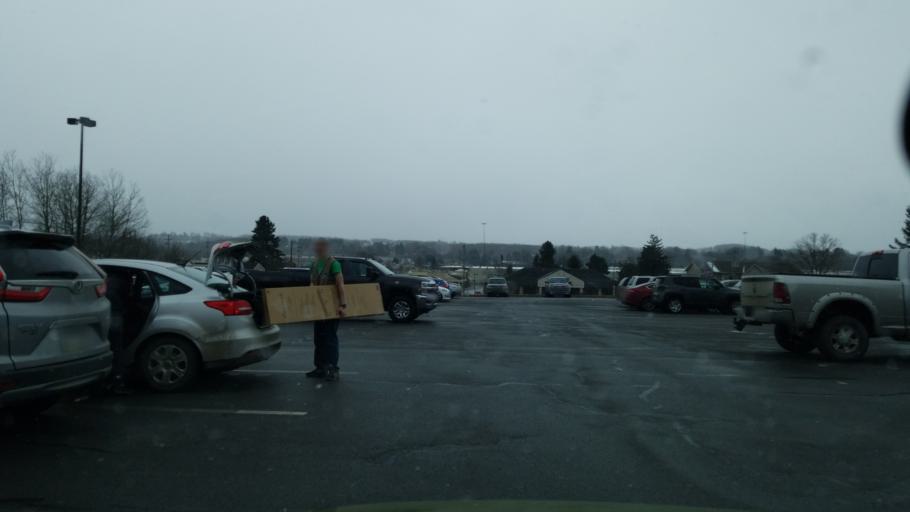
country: US
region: Pennsylvania
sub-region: Clearfield County
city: DuBois
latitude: 41.1254
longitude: -78.7296
